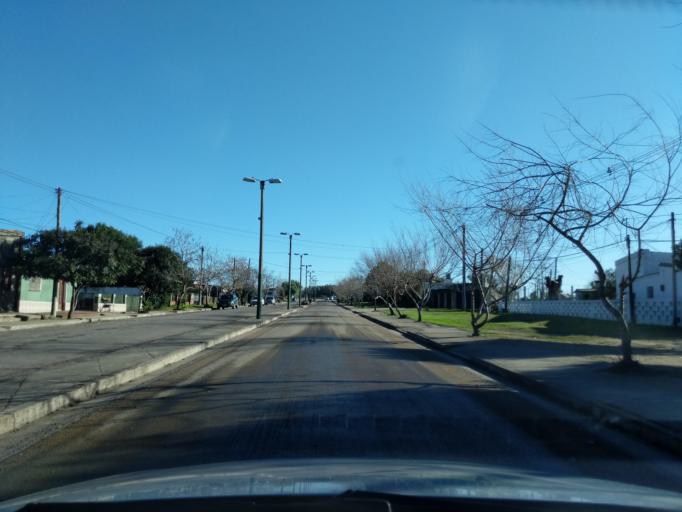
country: UY
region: Florida
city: Florida
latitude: -34.0933
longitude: -56.2376
